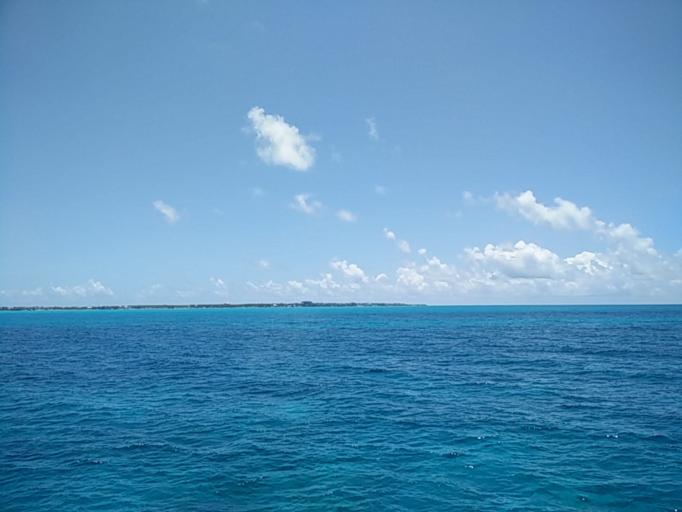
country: MX
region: Quintana Roo
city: Isla Mujeres
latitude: 21.2039
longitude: -86.7595
